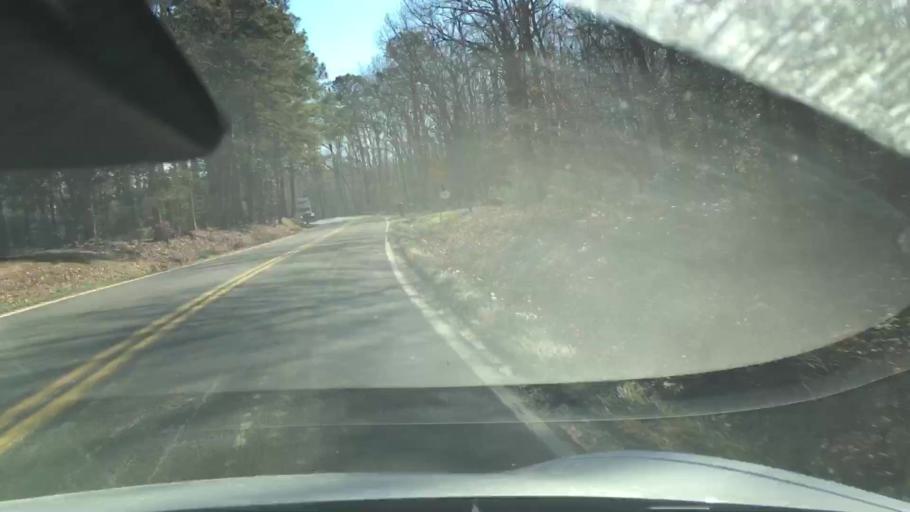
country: US
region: Virginia
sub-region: Henrico County
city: Short Pump
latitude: 37.5858
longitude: -77.7492
